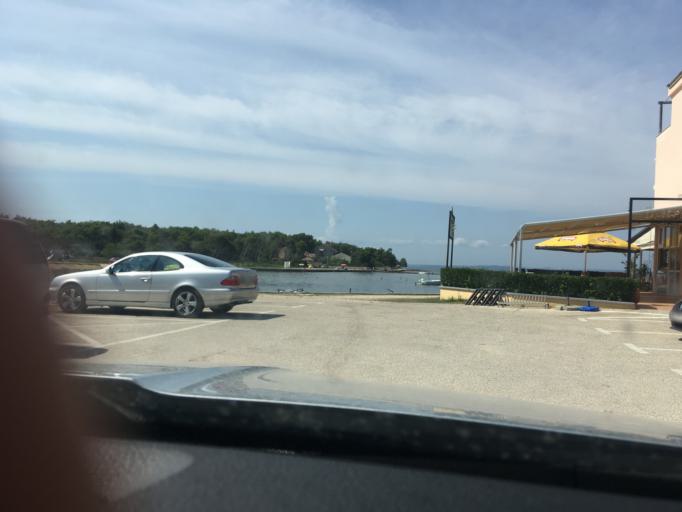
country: HR
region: Zadarska
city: Privlaka
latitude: 44.2557
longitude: 15.1282
